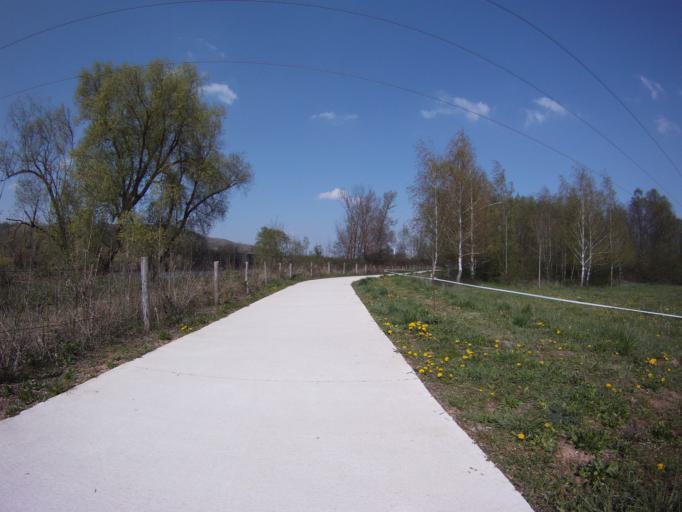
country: FR
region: Lorraine
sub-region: Departement de Meurthe-et-Moselle
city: Dieulouard
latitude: 48.8470
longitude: 6.0800
